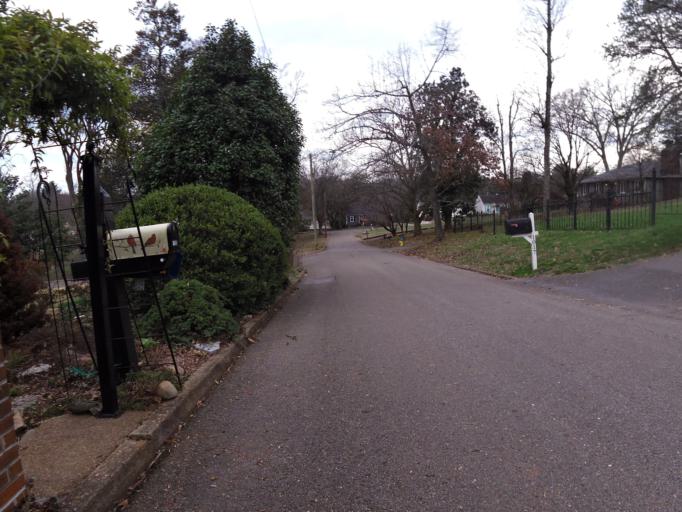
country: US
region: Tennessee
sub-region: Knox County
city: Knoxville
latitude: 35.9321
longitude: -83.9720
